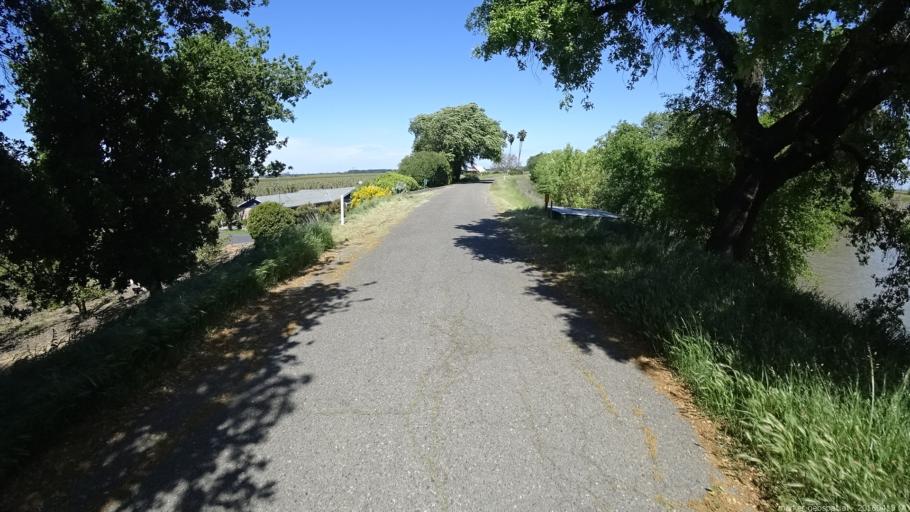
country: US
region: California
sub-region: Sacramento County
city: Walnut Grove
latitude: 38.2832
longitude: -121.5894
